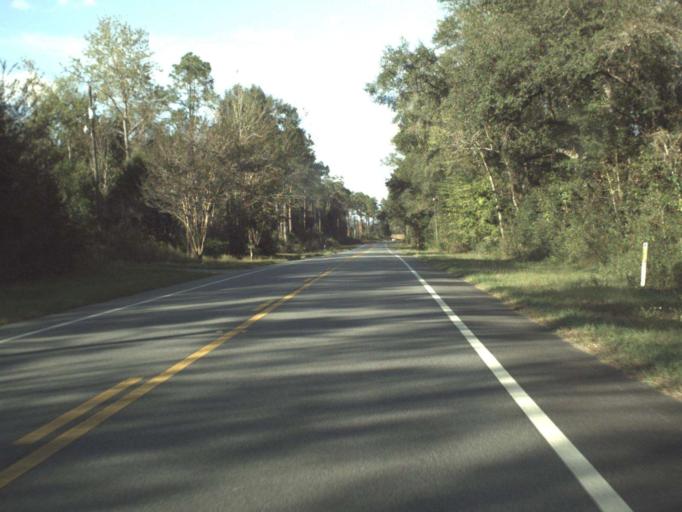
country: US
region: Florida
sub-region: Holmes County
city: Bonifay
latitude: 30.7164
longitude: -85.6165
